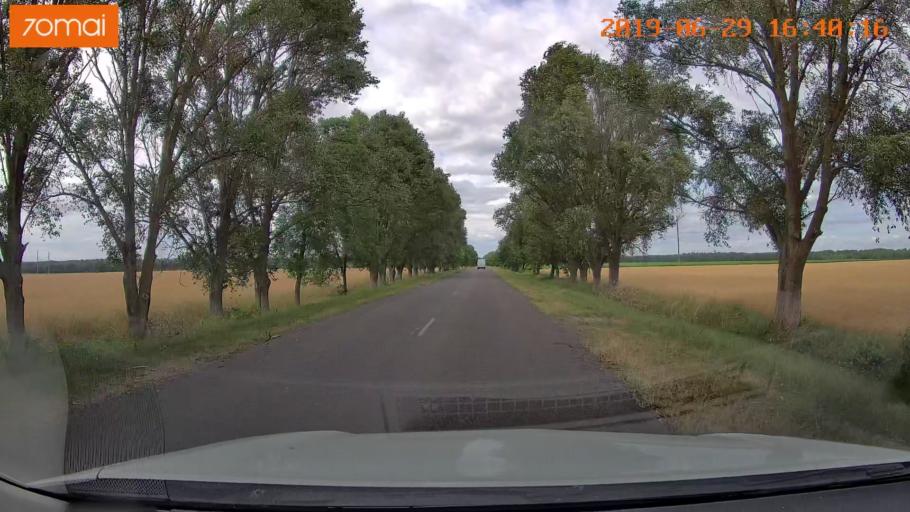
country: BY
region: Brest
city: Luninyets
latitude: 52.2535
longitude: 27.0170
